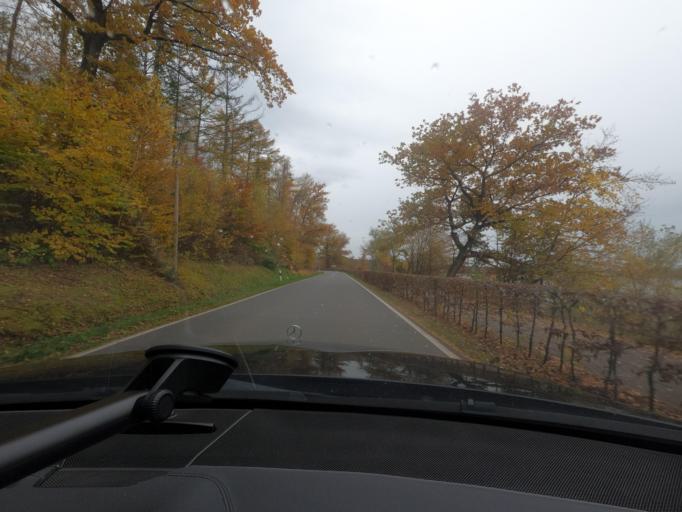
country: DE
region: North Rhine-Westphalia
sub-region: Regierungsbezirk Arnsberg
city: Mohnesee
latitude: 51.4815
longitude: 8.1103
